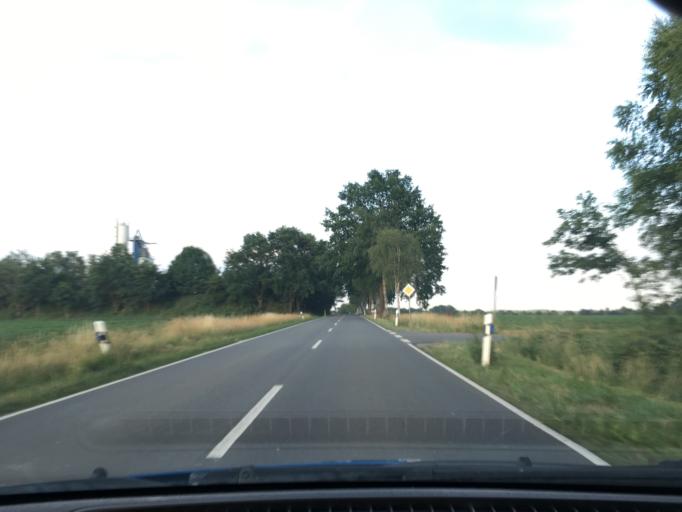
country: DE
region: Lower Saxony
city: Eschede
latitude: 52.7260
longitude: 10.2565
